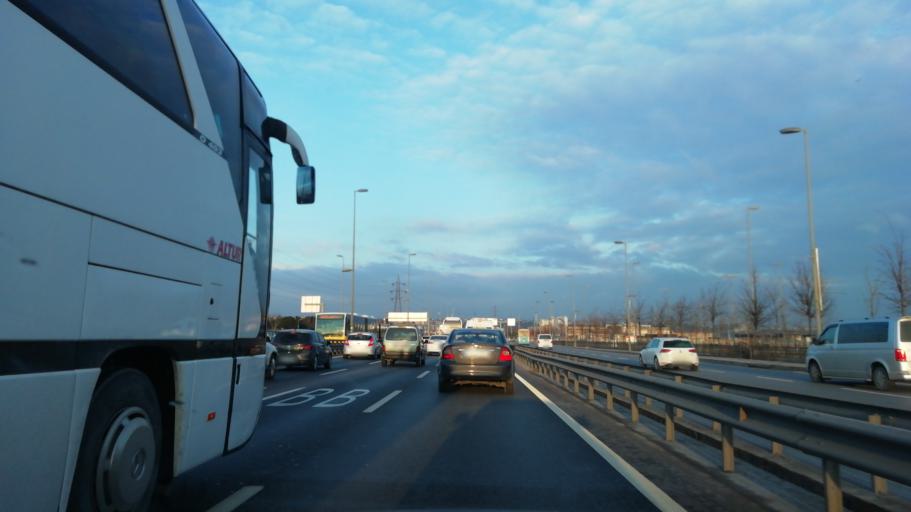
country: TR
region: Istanbul
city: Yakuplu
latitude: 40.9799
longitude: 28.7515
